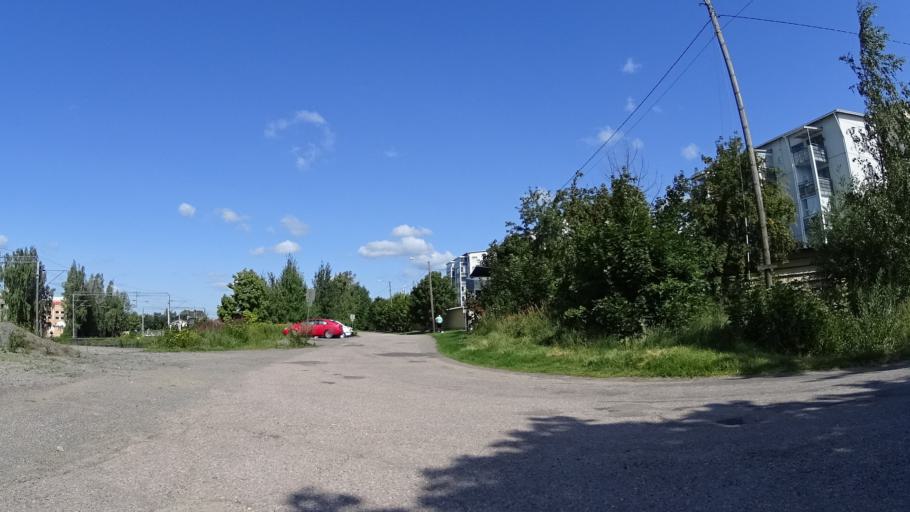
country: FI
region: Uusimaa
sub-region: Helsinki
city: Jaervenpaeae
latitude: 60.4712
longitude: 25.0955
